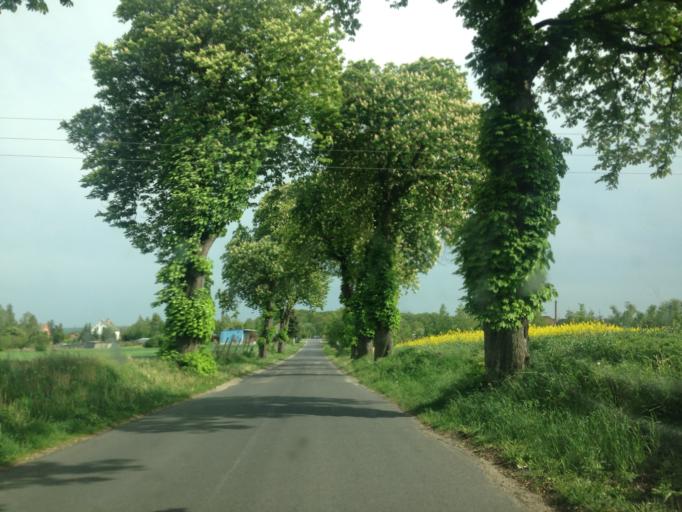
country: PL
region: Kujawsko-Pomorskie
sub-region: Powiat brodnicki
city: Brodnica
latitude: 53.2907
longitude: 19.4137
